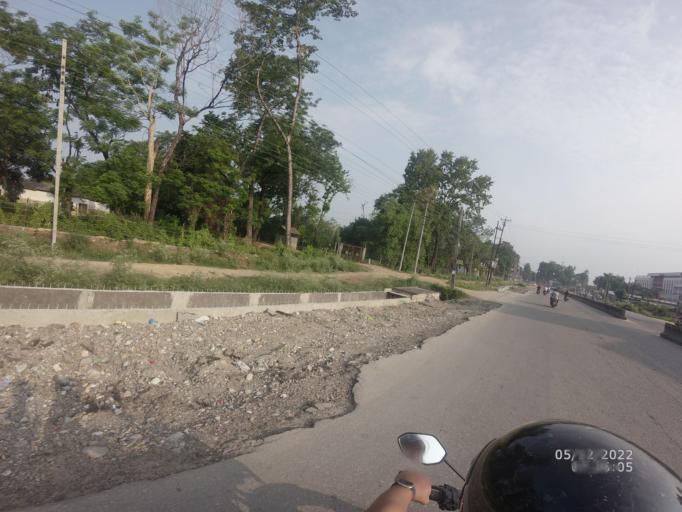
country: NP
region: Central Region
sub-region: Narayani Zone
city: Bharatpur
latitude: 27.6831
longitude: 84.4298
